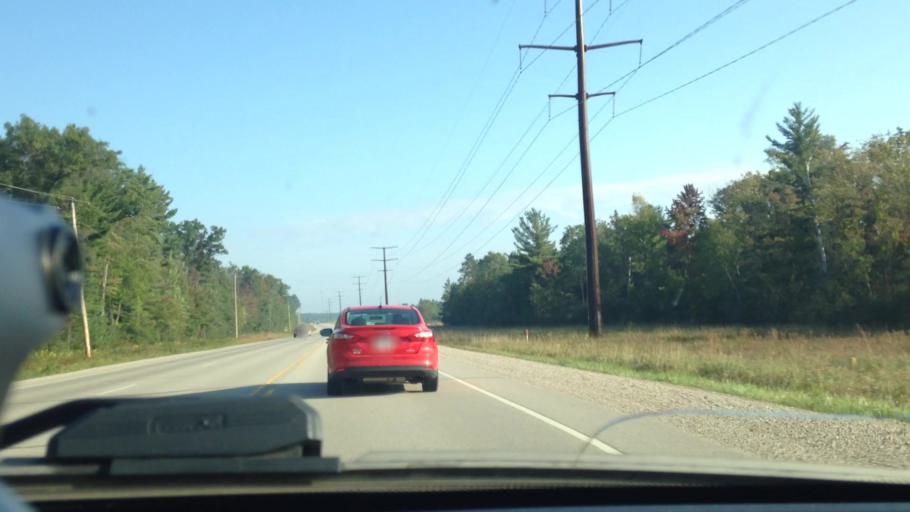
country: US
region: Wisconsin
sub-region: Marinette County
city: Peshtigo
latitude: 45.1929
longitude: -87.9948
